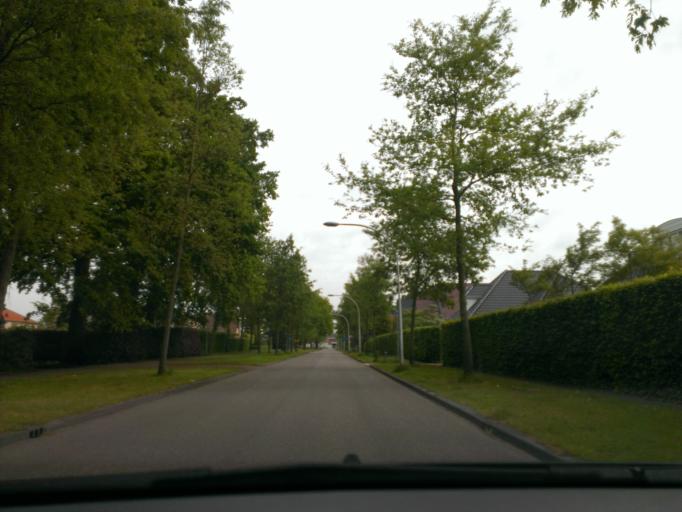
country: NL
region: Overijssel
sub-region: Gemeente Almelo
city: Almelo
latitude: 52.3342
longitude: 6.6639
